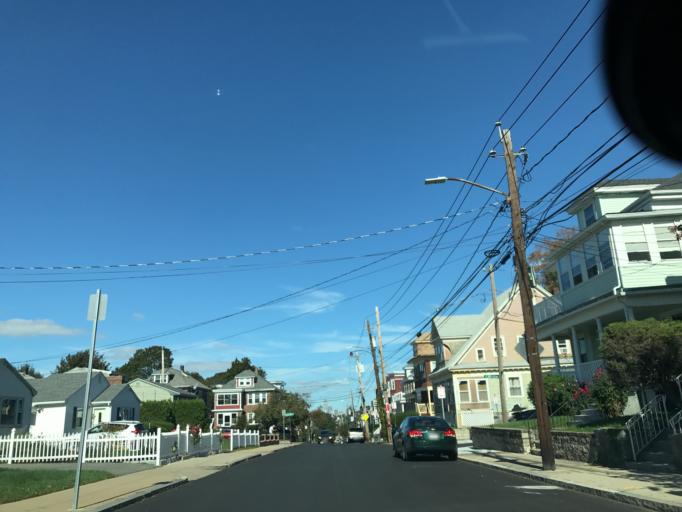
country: US
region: Massachusetts
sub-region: Suffolk County
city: South Boston
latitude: 42.2913
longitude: -71.0535
